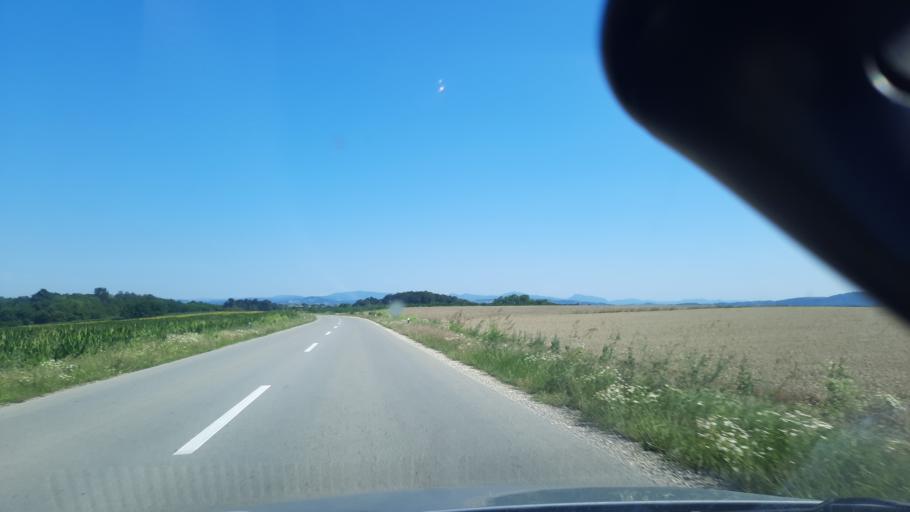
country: RS
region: Central Serbia
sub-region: Branicevski Okrug
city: Malo Crnice
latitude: 44.5617
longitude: 21.4355
